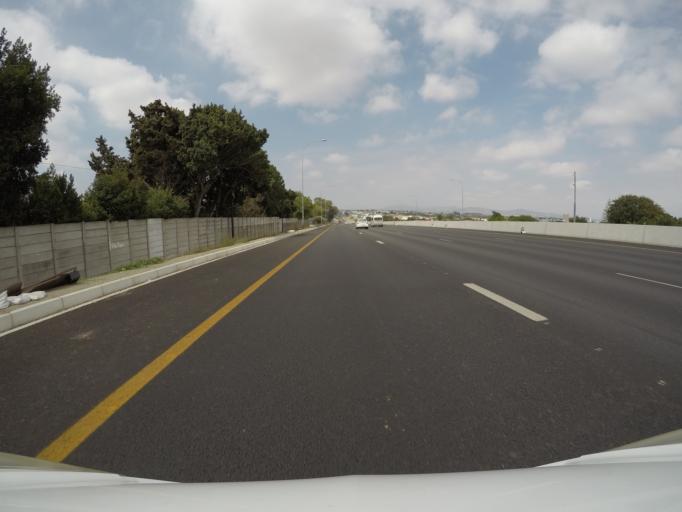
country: ZA
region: Western Cape
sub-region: City of Cape Town
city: Kraaifontein
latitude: -33.8885
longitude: 18.6206
